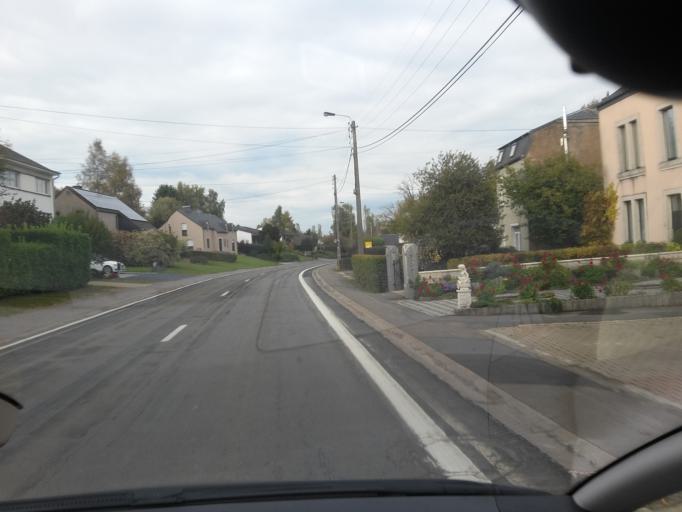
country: BE
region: Wallonia
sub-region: Province du Luxembourg
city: Arlon
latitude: 49.6958
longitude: 5.8196
